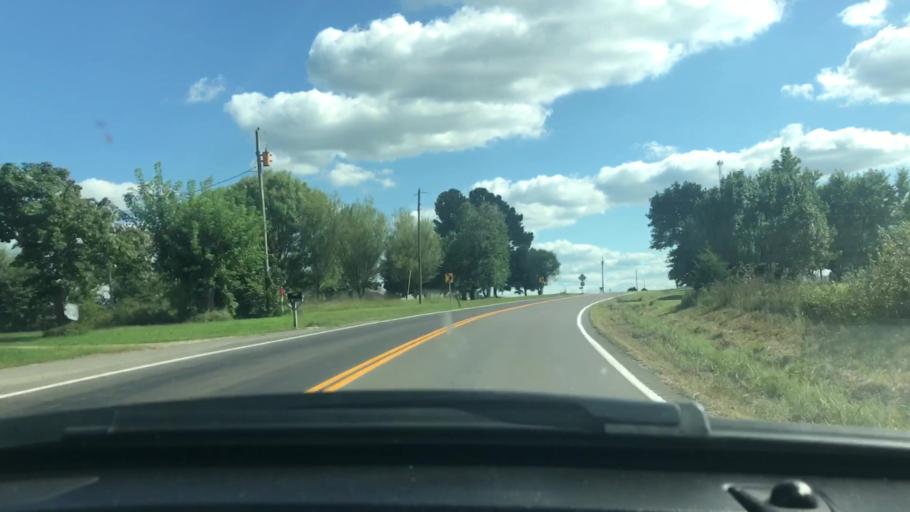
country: US
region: Missouri
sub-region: Wright County
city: Mountain Grove
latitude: 37.2523
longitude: -92.3004
